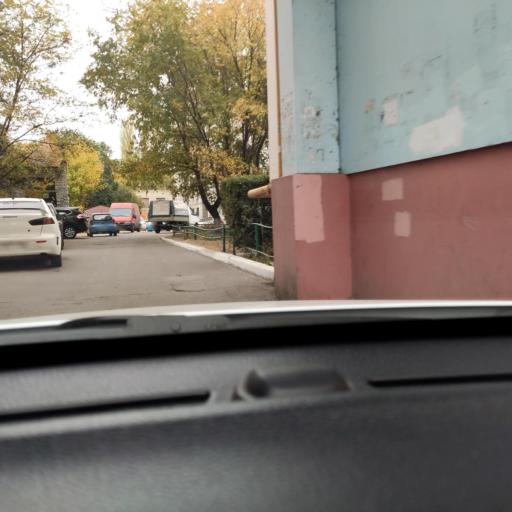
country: RU
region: Voronezj
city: Voronezh
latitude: 51.6550
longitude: 39.2404
